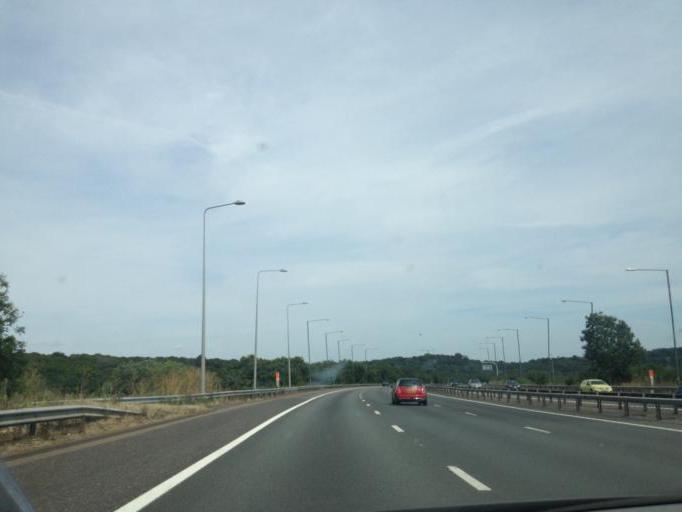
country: GB
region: England
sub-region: Hertfordshire
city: Borehamwood
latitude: 51.6380
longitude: -0.2797
